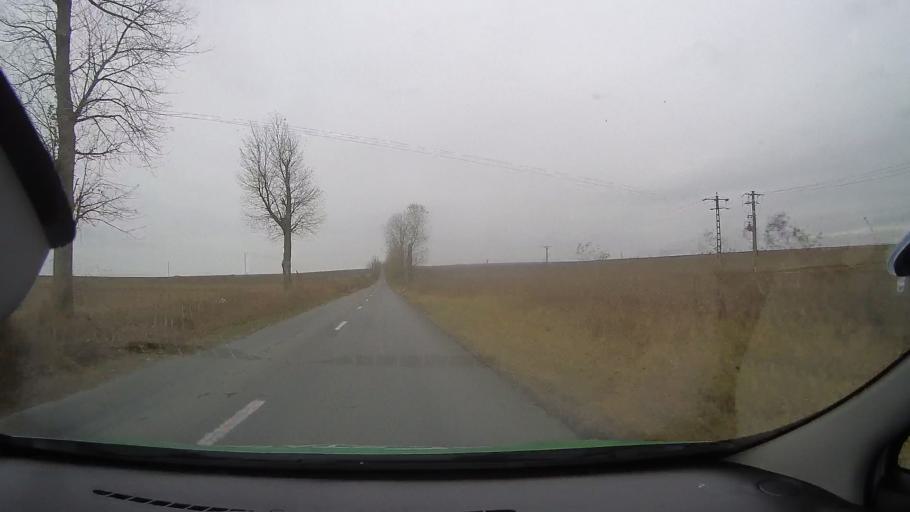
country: RO
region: Constanta
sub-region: Comuna Pantelimon
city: Pantelimon
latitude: 44.5533
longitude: 28.3268
